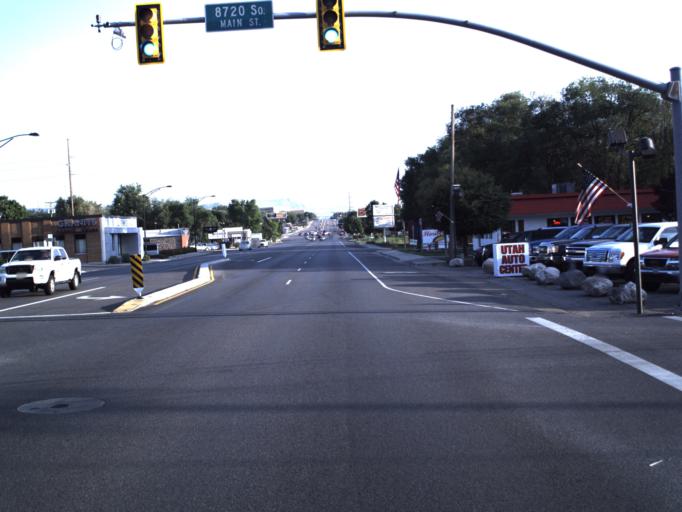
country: US
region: Utah
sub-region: Salt Lake County
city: Sandy City
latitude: 40.5932
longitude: -111.8910
